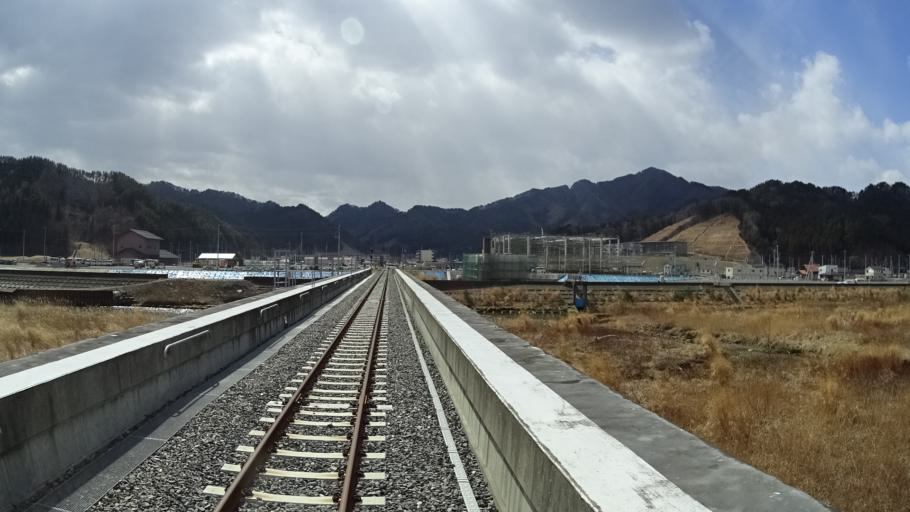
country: JP
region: Iwate
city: Otsuchi
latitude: 39.3300
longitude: 141.8896
